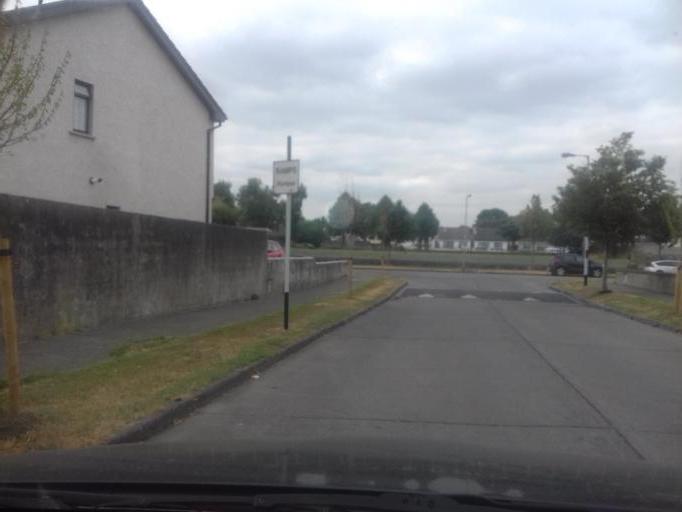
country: IE
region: Leinster
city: Hartstown
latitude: 53.3989
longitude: -6.4117
